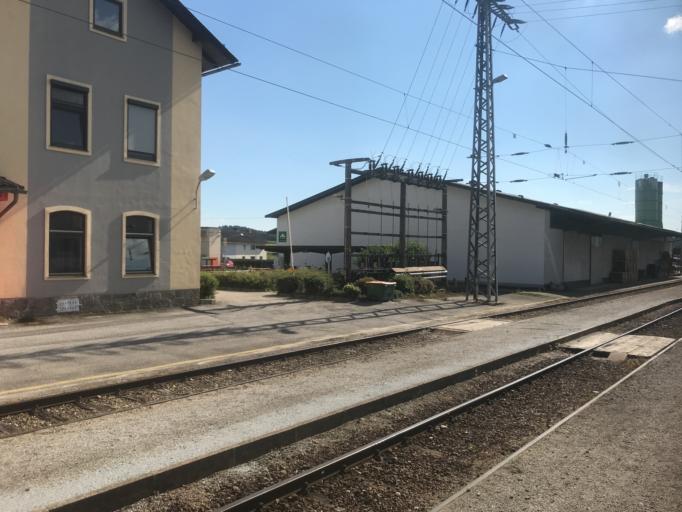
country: AT
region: Upper Austria
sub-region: Politischer Bezirk Urfahr-Umgebung
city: Reichenthal
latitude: 48.5572
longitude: 14.4492
